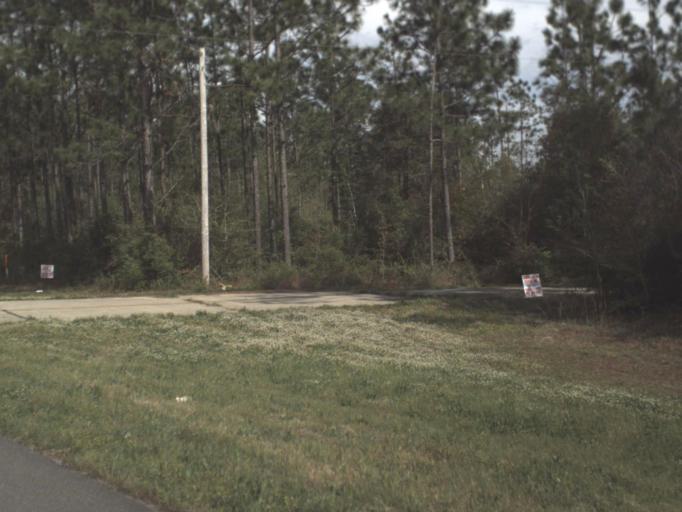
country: US
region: Florida
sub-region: Santa Rosa County
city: East Milton
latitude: 30.6861
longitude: -86.8263
